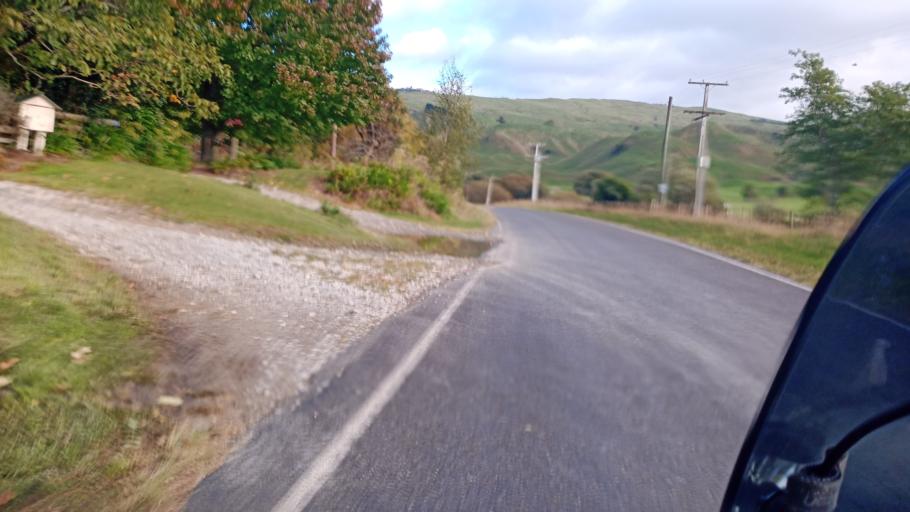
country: NZ
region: Gisborne
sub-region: Gisborne District
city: Gisborne
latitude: -38.5397
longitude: 177.5859
